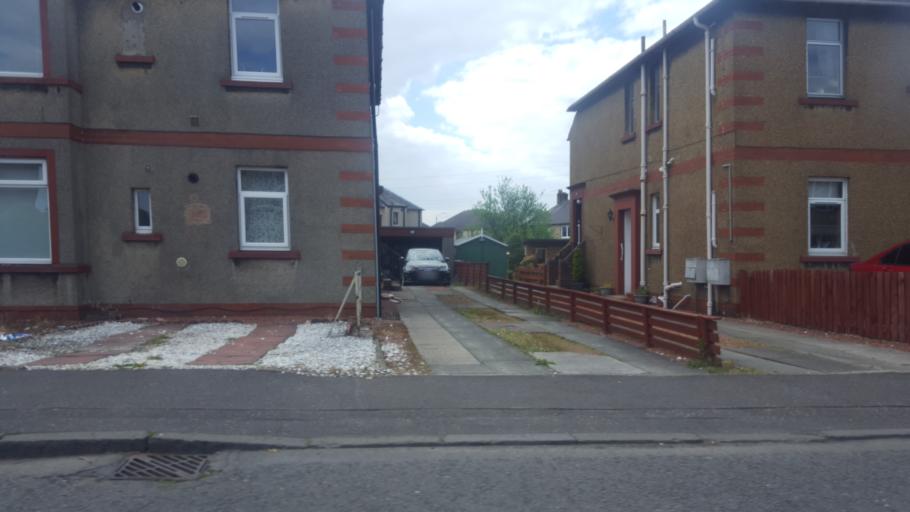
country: GB
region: Scotland
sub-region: Falkirk
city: Grangemouth
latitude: 56.0119
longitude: -3.7244
